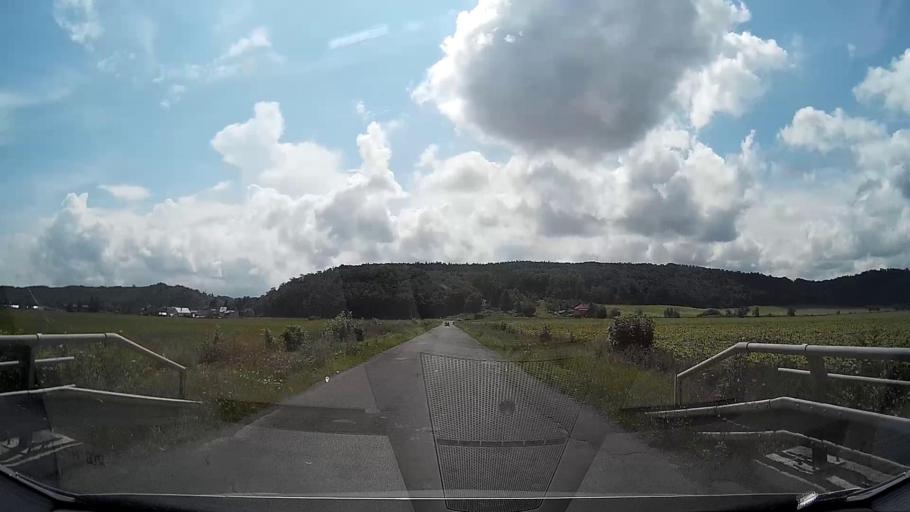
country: SK
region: Banskobystricky
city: Fil'akovo
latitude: 48.2931
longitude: 19.7906
